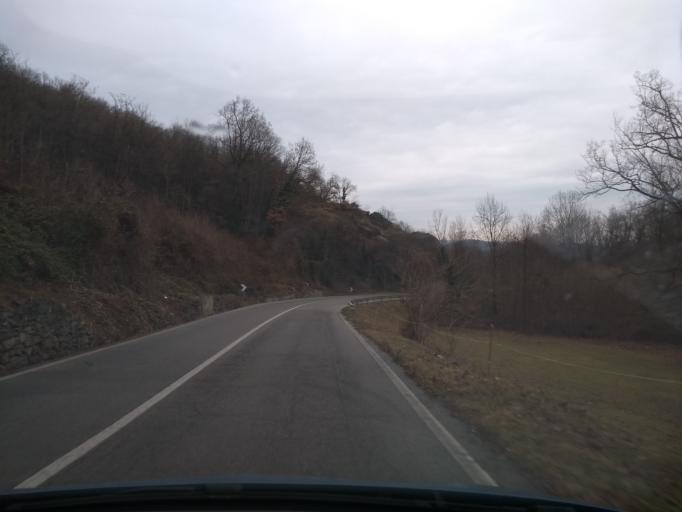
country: IT
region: Piedmont
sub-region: Provincia di Torino
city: Colleretto Giacosa
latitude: 45.4366
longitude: 7.8013
